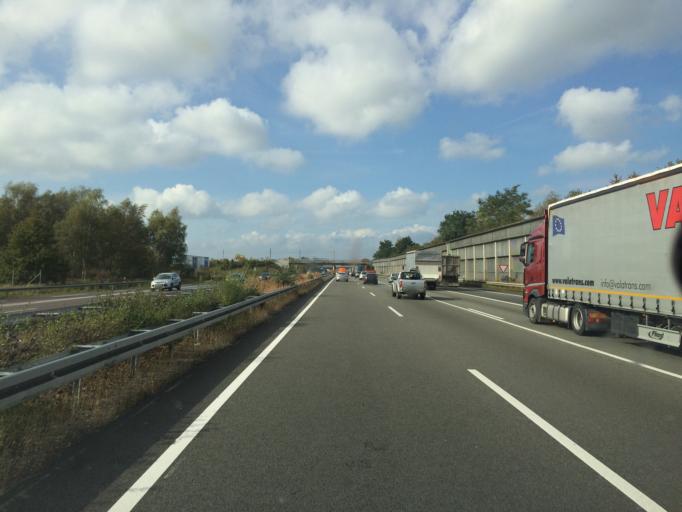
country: DE
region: Lower Saxony
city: Vordorf
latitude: 52.3157
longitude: 10.5121
